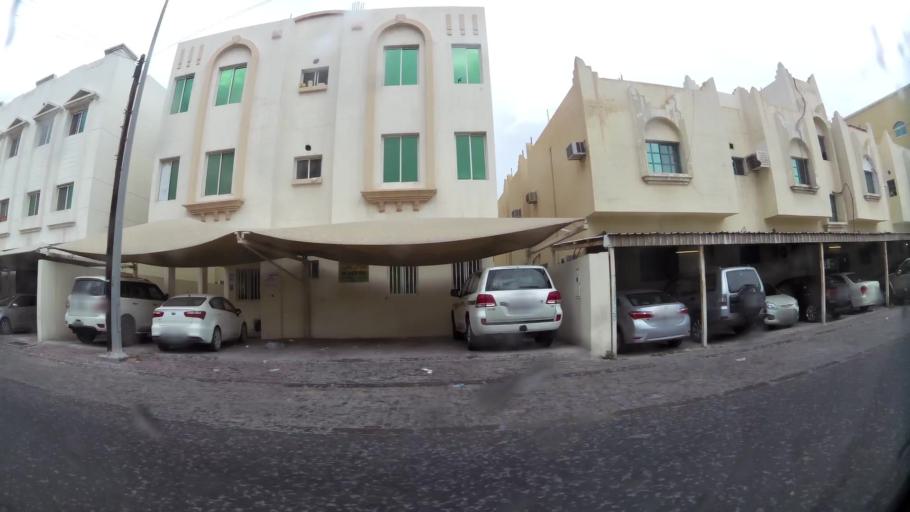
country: QA
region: Baladiyat ad Dawhah
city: Doha
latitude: 25.2748
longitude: 51.4909
